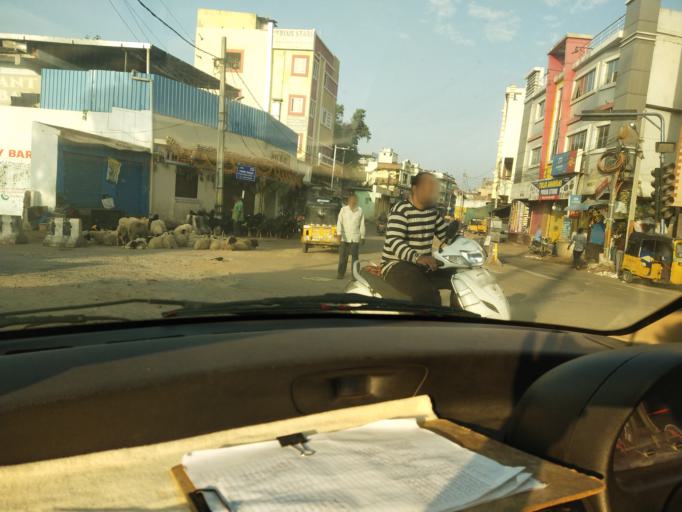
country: IN
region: Telangana
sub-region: Hyderabad
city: Hyderabad
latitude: 17.3686
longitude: 78.4577
